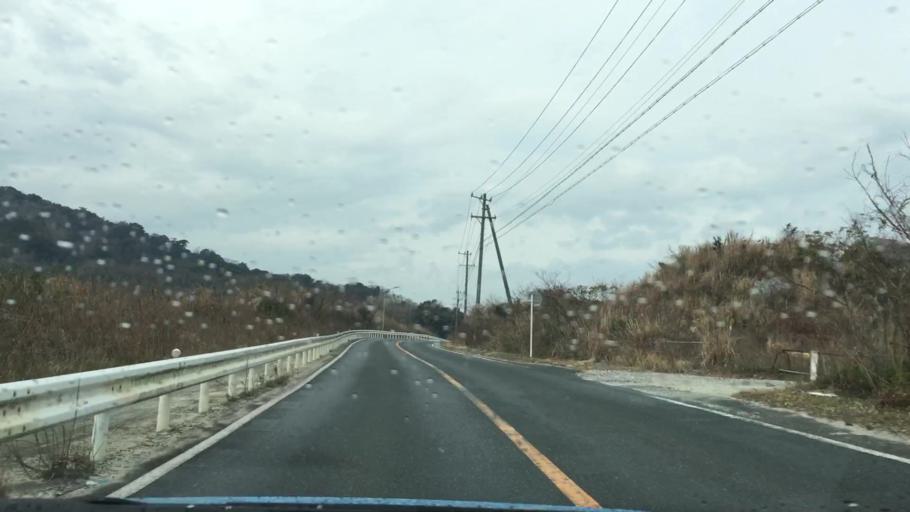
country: JP
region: Aichi
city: Tahara
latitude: 34.6835
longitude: 137.2500
